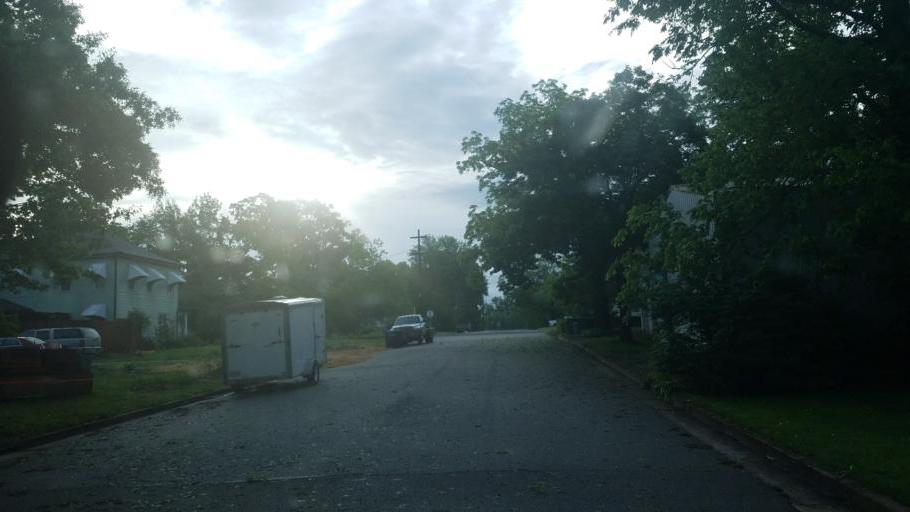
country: US
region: Missouri
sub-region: Moniteau County
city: California
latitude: 38.6248
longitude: -92.5703
